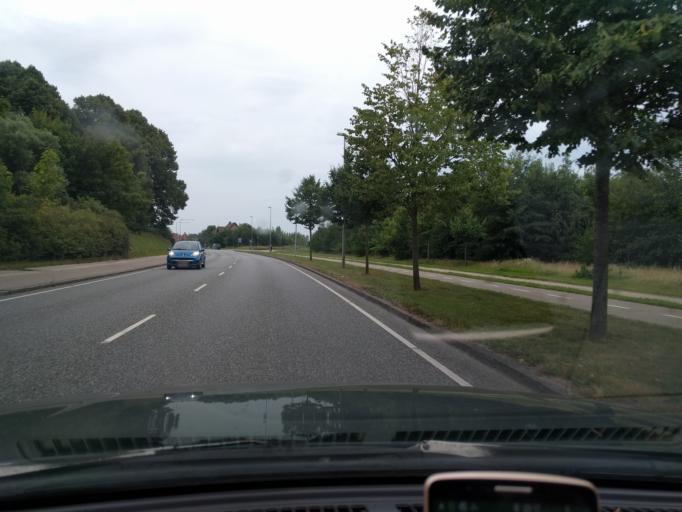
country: DK
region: Zealand
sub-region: Slagelse Kommune
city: Korsor
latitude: 55.3462
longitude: 11.1406
